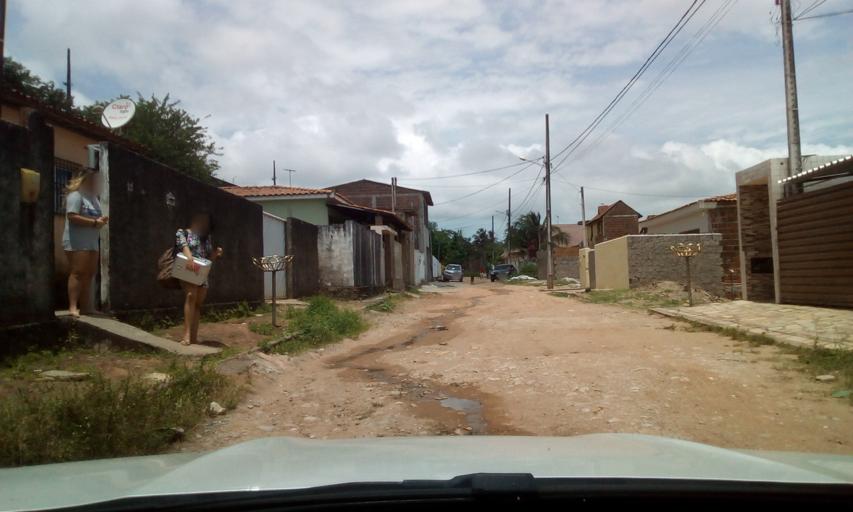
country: BR
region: Paraiba
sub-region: Joao Pessoa
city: Joao Pessoa
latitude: -7.1705
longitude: -34.8842
